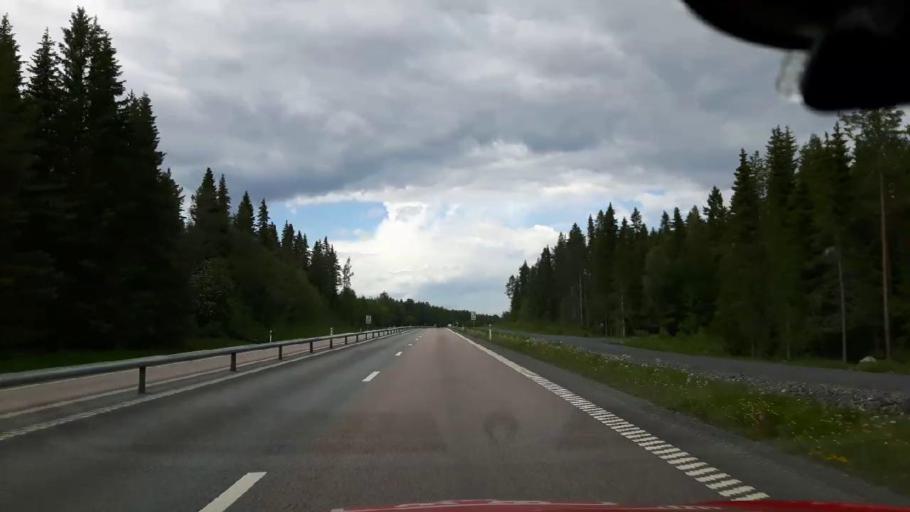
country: SE
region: Jaemtland
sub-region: OEstersunds Kommun
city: Ostersund
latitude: 63.2539
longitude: 14.5722
